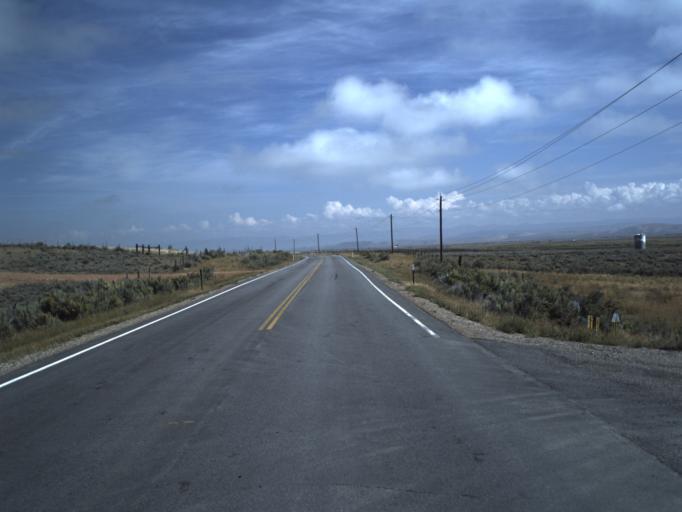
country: US
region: Utah
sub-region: Rich County
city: Randolph
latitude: 41.7625
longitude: -111.1306
